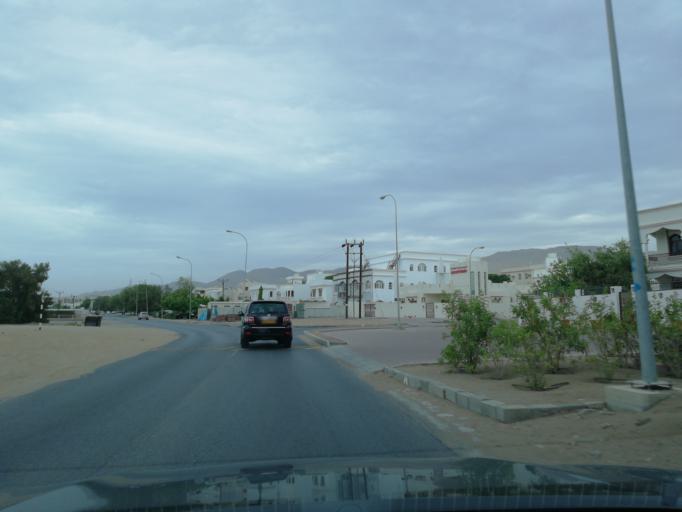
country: OM
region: Muhafazat Masqat
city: Bawshar
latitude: 23.5802
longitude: 58.3950
